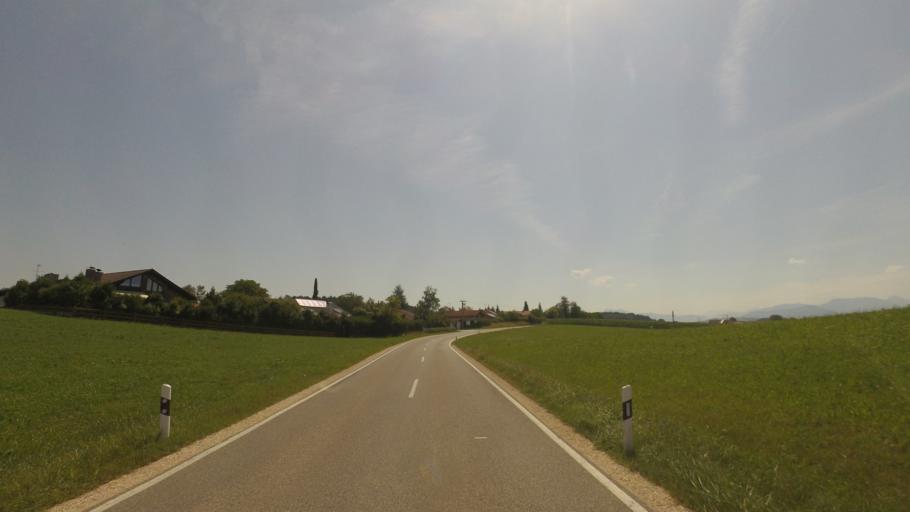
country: DE
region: Bavaria
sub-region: Upper Bavaria
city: Nussdorf
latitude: 47.9028
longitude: 12.5991
